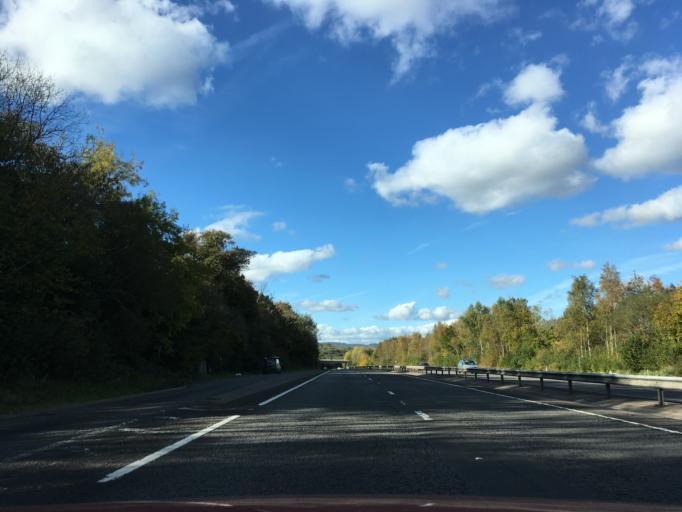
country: GB
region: Wales
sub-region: Merthyr Tydfil County Borough
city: Abercanaid
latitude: 51.7220
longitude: -3.3689
